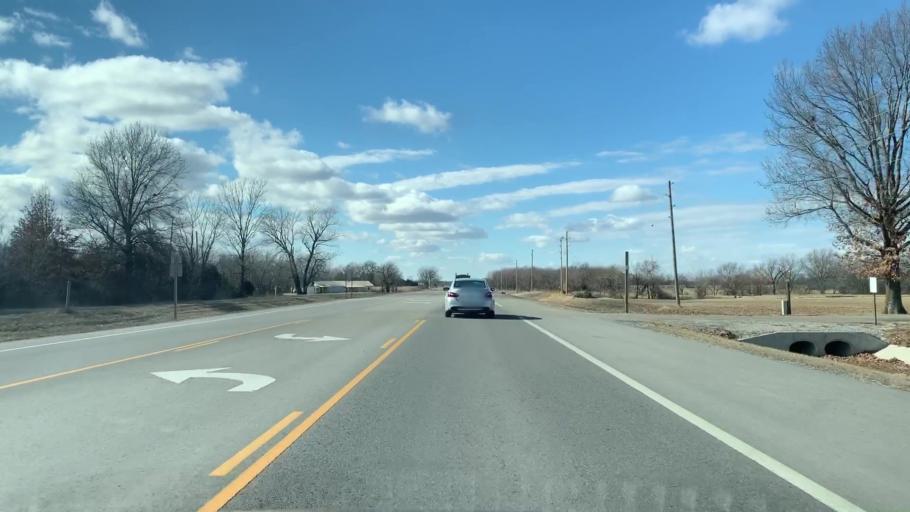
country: US
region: Kansas
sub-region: Crawford County
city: Pittsburg
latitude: 37.3397
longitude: -94.8372
